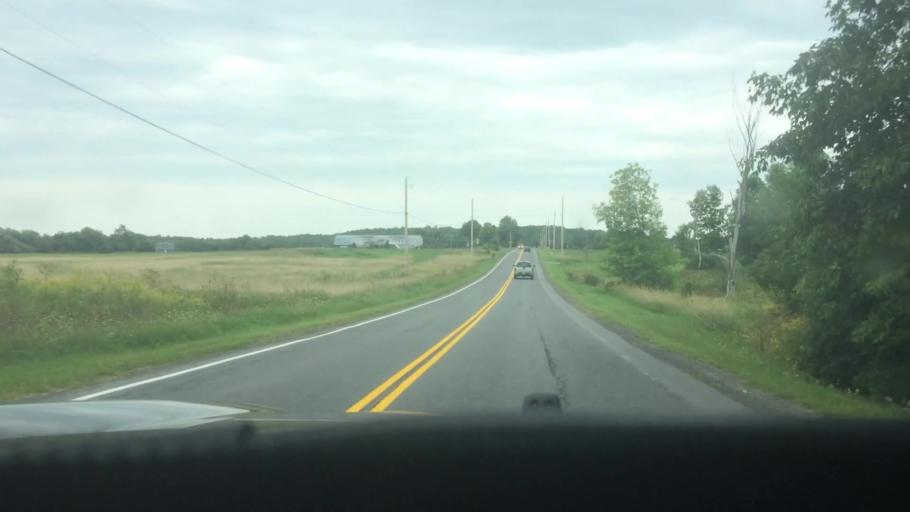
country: US
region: New York
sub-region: St. Lawrence County
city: Canton
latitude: 44.5507
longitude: -75.1419
